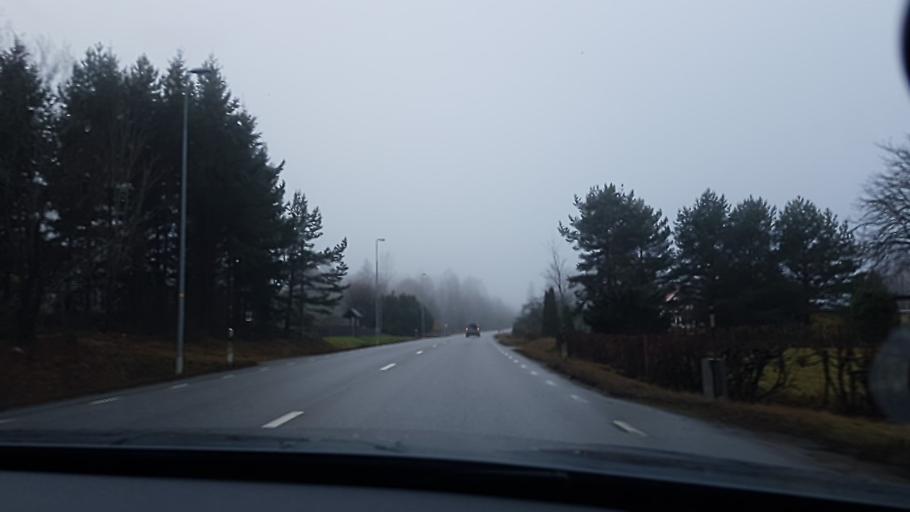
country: SE
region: Vaestra Goetaland
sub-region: Gullspangs Kommun
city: Gullspang
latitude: 58.9761
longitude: 14.0802
